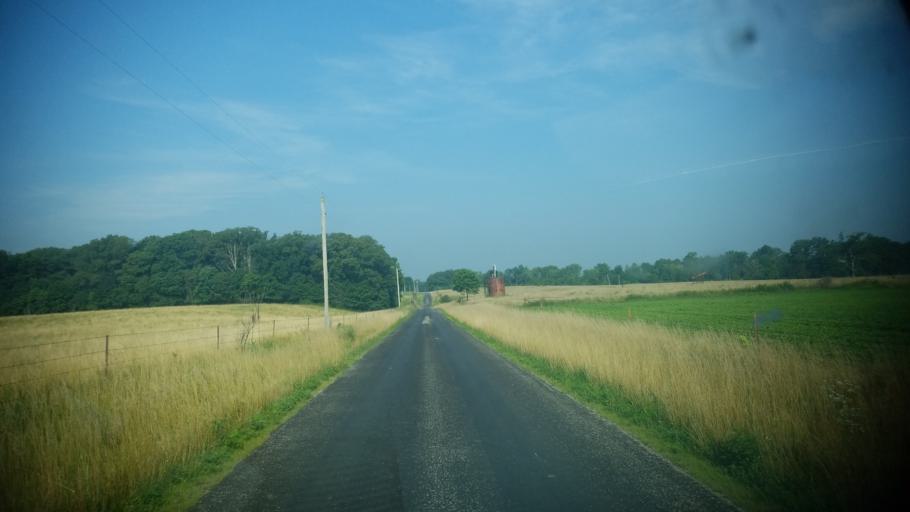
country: US
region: Illinois
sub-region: Clay County
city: Flora
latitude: 38.6027
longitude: -88.3958
